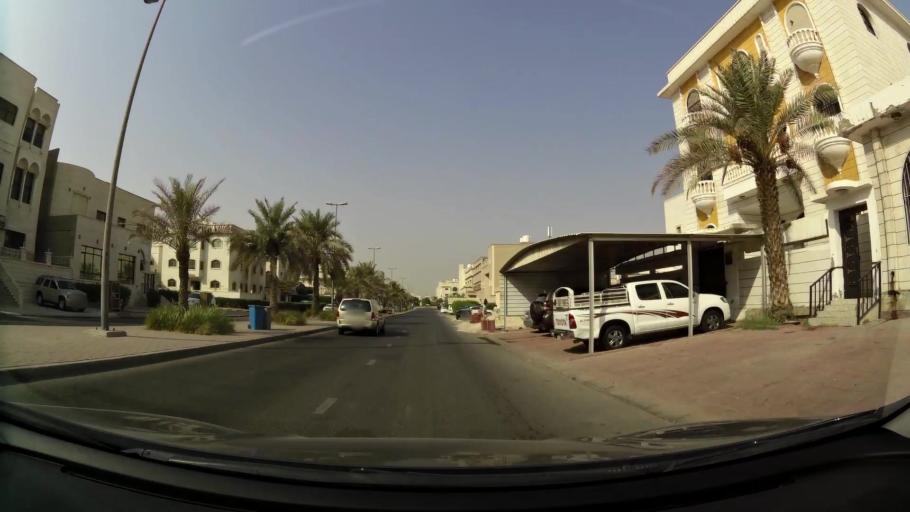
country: KW
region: Al Asimah
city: Ar Rabiyah
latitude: 29.2690
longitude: 47.8723
